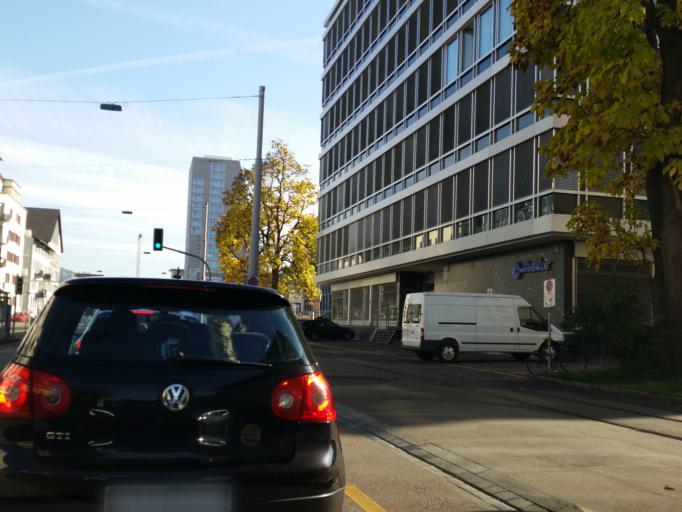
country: CH
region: Zurich
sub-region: Bezirk Zuerich
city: Zuerich (Kreis 5) / Escher-Wyss
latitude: 47.3923
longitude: 8.5166
